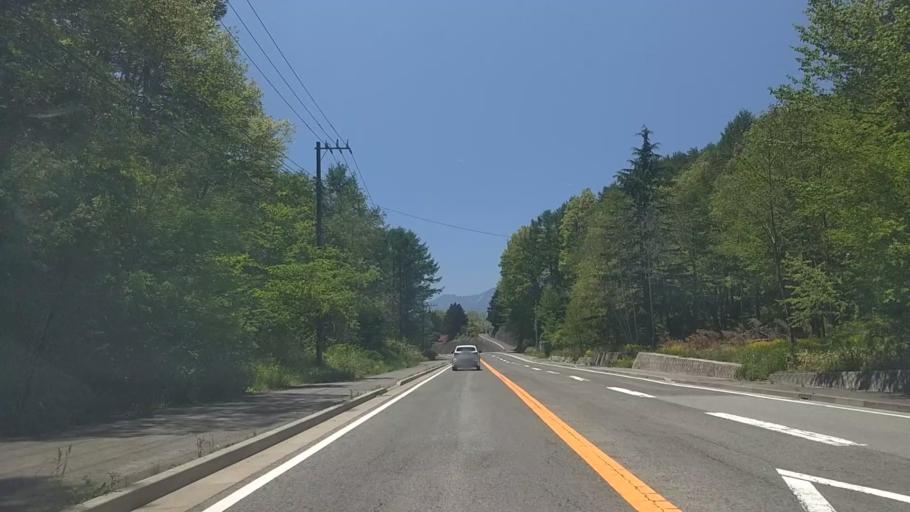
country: JP
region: Yamanashi
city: Nirasaki
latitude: 35.9006
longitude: 138.4425
